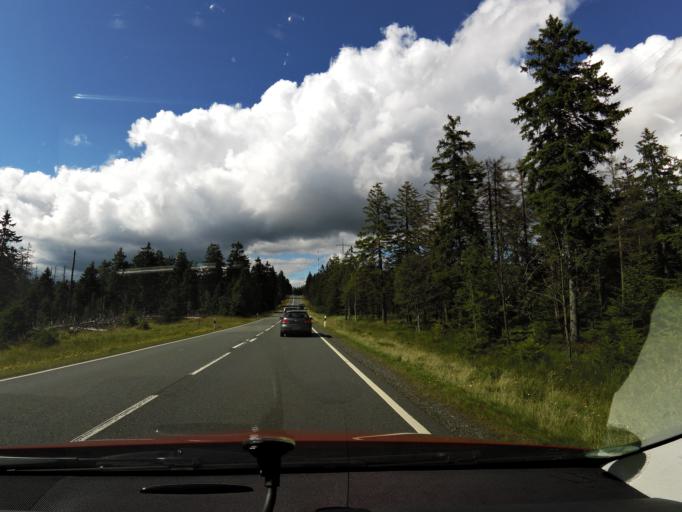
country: DE
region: Lower Saxony
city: Sankt Andreasberg
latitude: 51.7906
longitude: 10.5461
